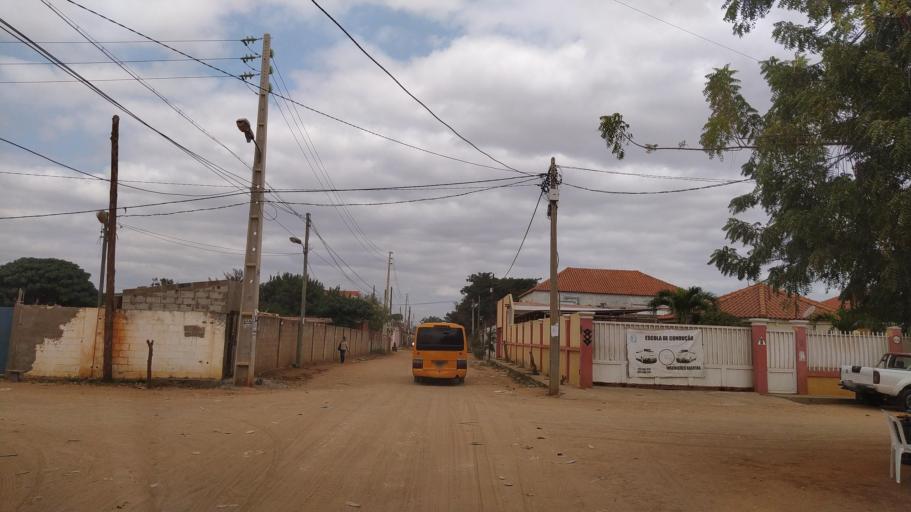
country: AO
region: Luanda
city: Luanda
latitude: -8.9265
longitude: 13.2614
